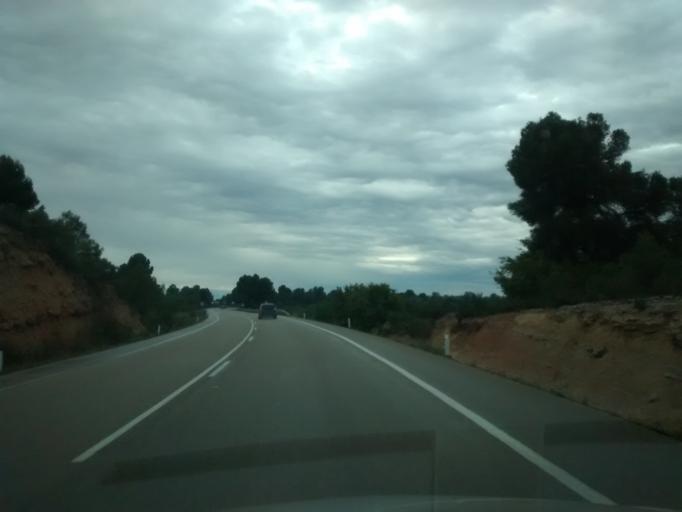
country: ES
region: Aragon
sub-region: Provincia de Zaragoza
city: Maella
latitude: 41.1528
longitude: 0.1006
